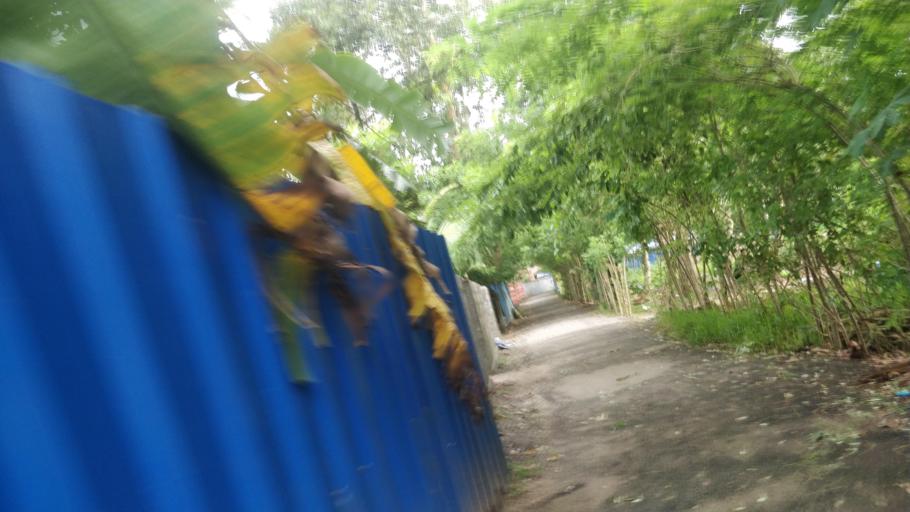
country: IN
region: Kerala
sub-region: Alappuzha
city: Shertallai
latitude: 9.6914
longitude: 76.3602
